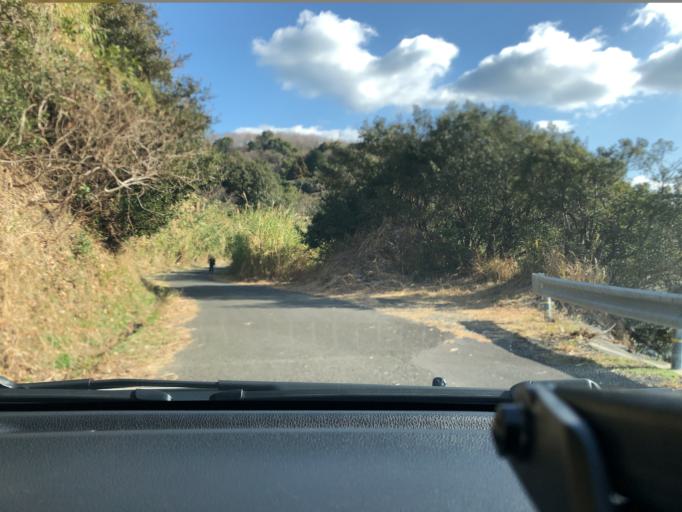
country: JP
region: Kochi
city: Sukumo
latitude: 32.9128
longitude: 132.6914
